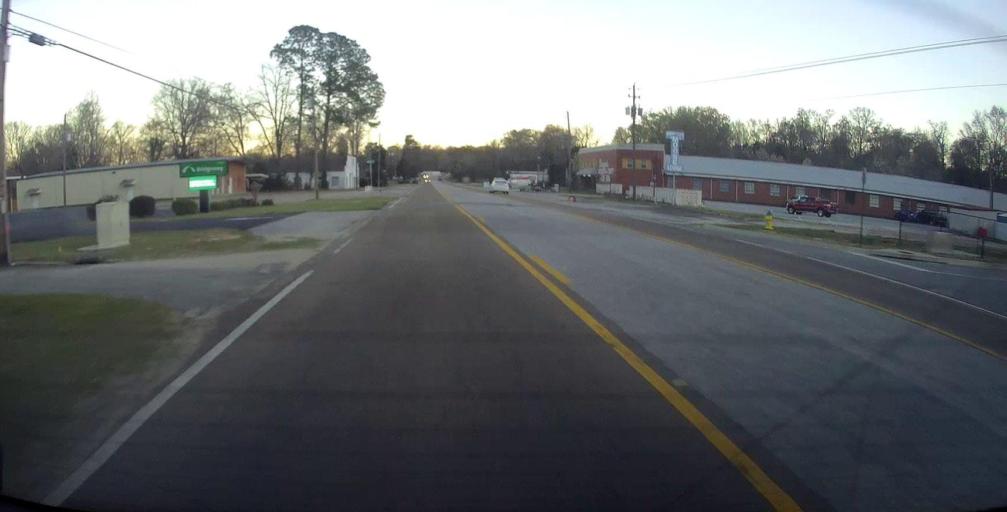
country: US
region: Alabama
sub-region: Russell County
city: Phenix City
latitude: 32.4785
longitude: -85.0267
